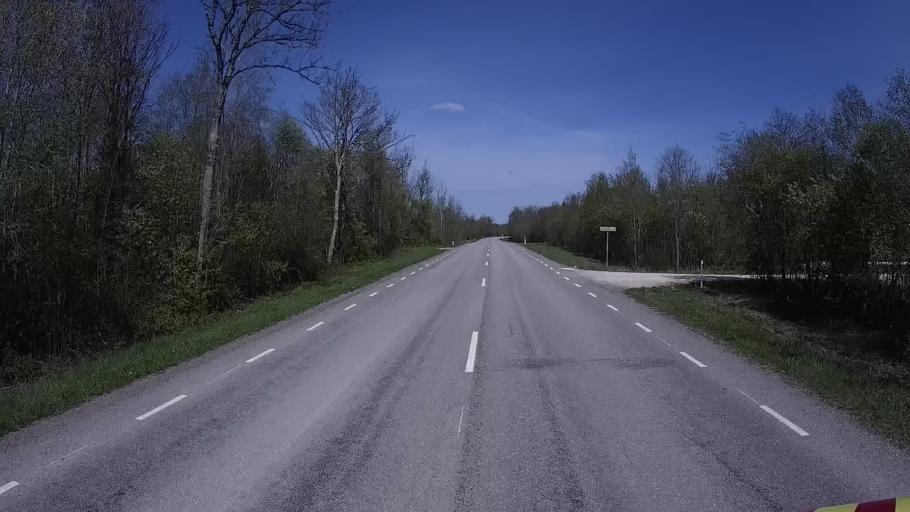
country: EE
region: Laeaene
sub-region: Ridala Parish
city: Uuemoisa
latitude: 58.9708
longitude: 23.6770
